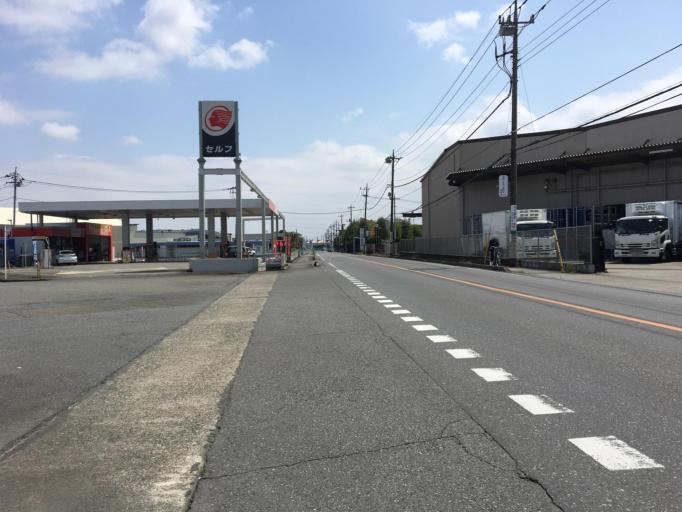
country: JP
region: Gunma
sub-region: Sawa-gun
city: Tamamura
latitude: 36.2956
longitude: 139.1386
